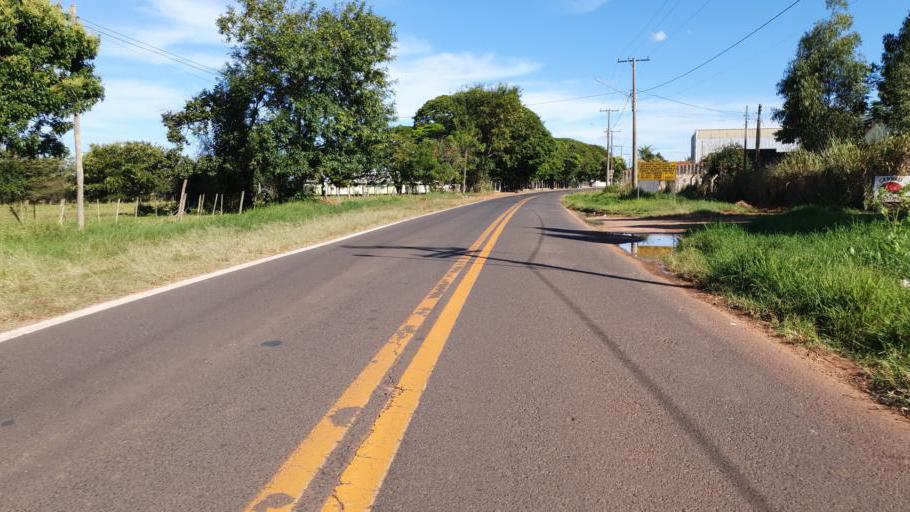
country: BR
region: Sao Paulo
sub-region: Paraguacu Paulista
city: Paraguacu Paulista
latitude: -22.4032
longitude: -50.5711
